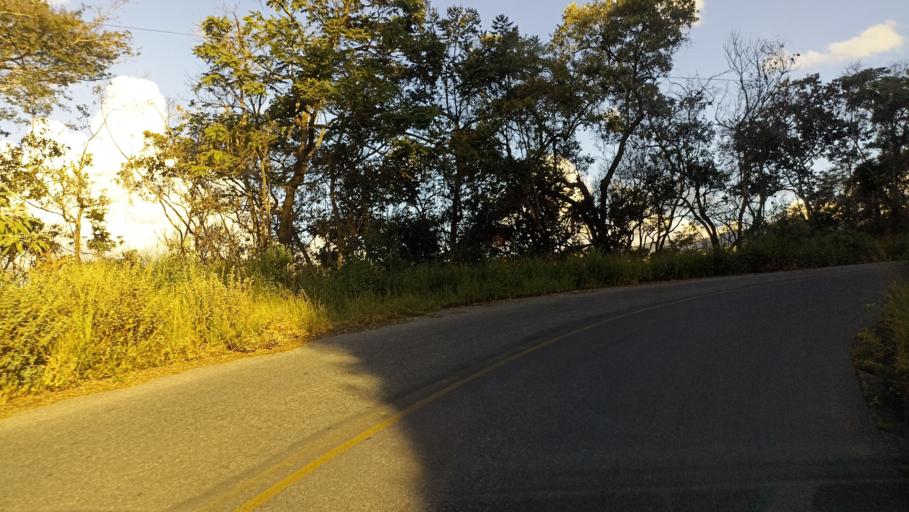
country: BR
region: Minas Gerais
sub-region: Ouro Preto
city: Ouro Preto
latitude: -20.3238
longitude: -43.6203
